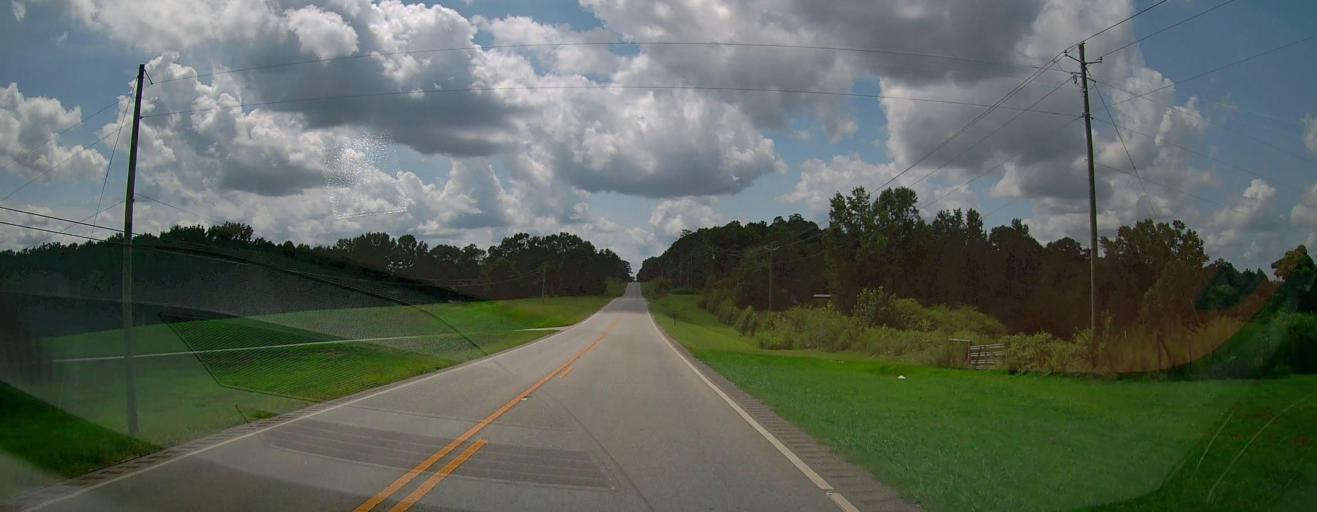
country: US
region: Georgia
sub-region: Carroll County
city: Bowdon
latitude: 33.5359
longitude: -85.3707
